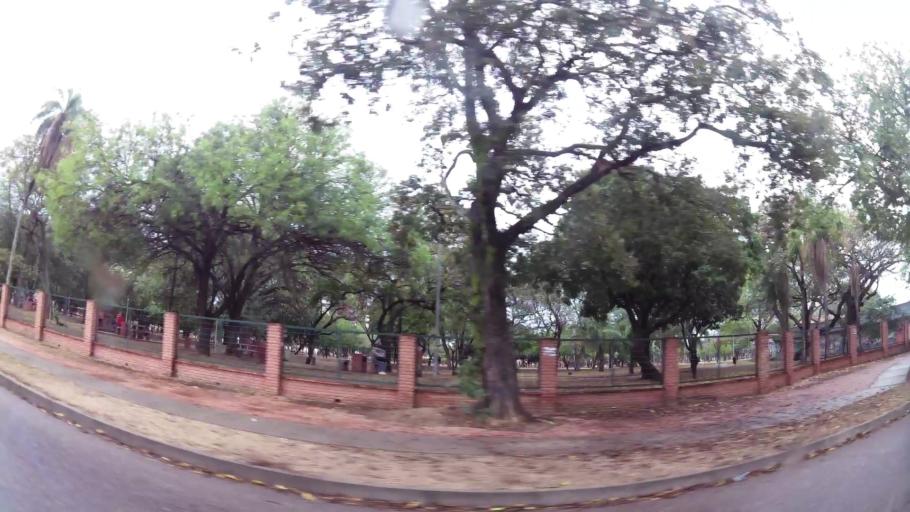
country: BO
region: Santa Cruz
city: Santa Cruz de la Sierra
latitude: -17.7930
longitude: -63.1699
